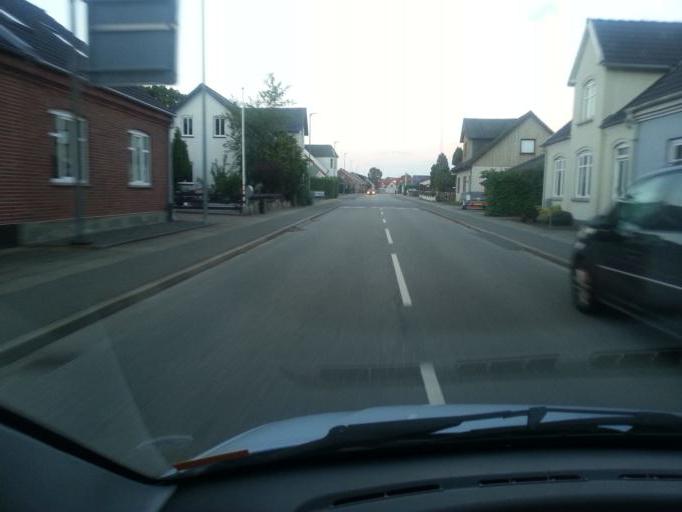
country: DK
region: South Denmark
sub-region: Varde Kommune
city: Olgod
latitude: 55.8087
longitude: 8.6113
